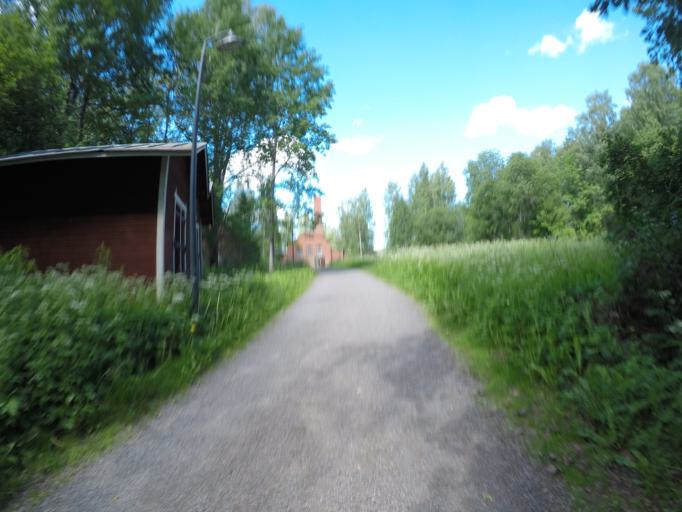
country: FI
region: Haeme
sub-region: Haemeenlinna
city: Haemeenlinna
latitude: 61.0034
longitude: 24.4676
